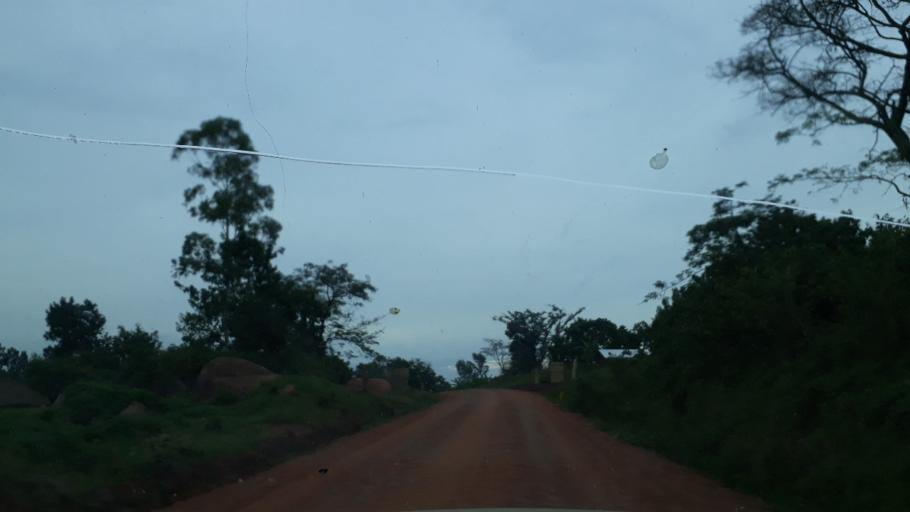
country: UG
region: Northern Region
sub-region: Zombo District
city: Paidha
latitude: 2.1861
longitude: 30.7268
